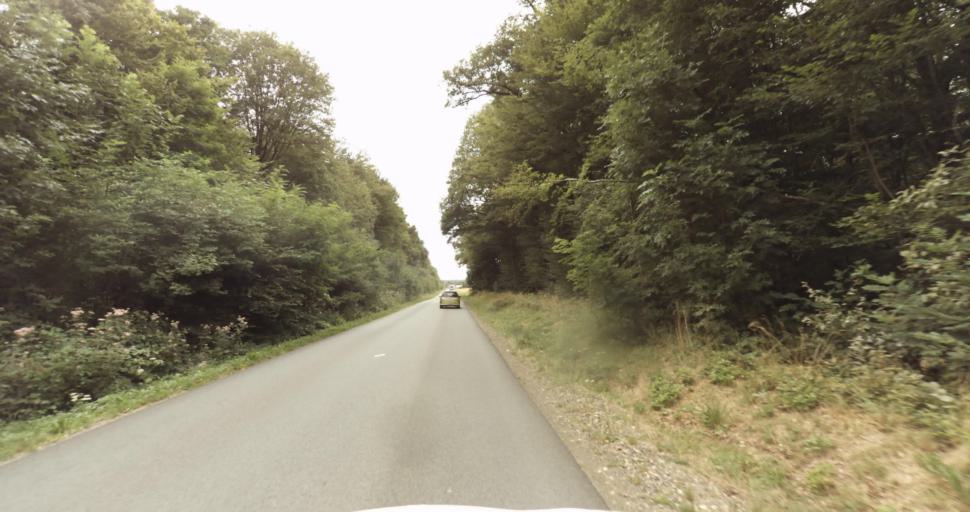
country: FR
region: Haute-Normandie
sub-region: Departement de l'Eure
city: Arnieres-sur-Iton
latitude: 48.9650
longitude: 1.1124
